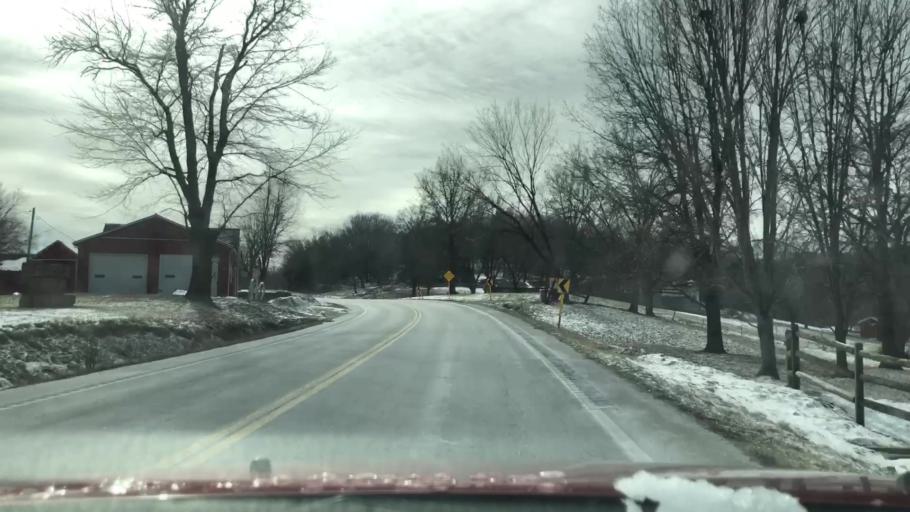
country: US
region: Missouri
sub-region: Jackson County
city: Oak Grove
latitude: 38.9403
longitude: -94.1325
